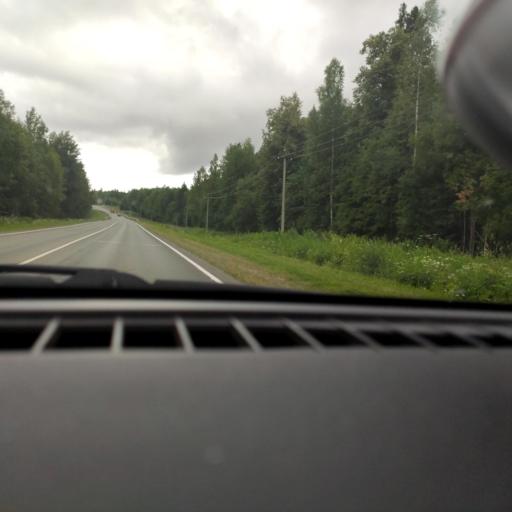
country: RU
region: Perm
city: Polazna
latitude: 58.3100
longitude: 56.1524
